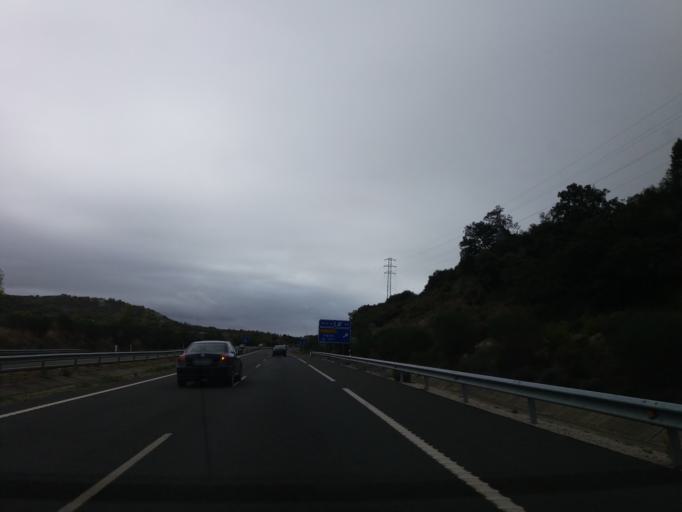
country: ES
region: Navarre
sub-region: Provincia de Navarra
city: Yerri
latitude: 42.6746
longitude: -1.9464
